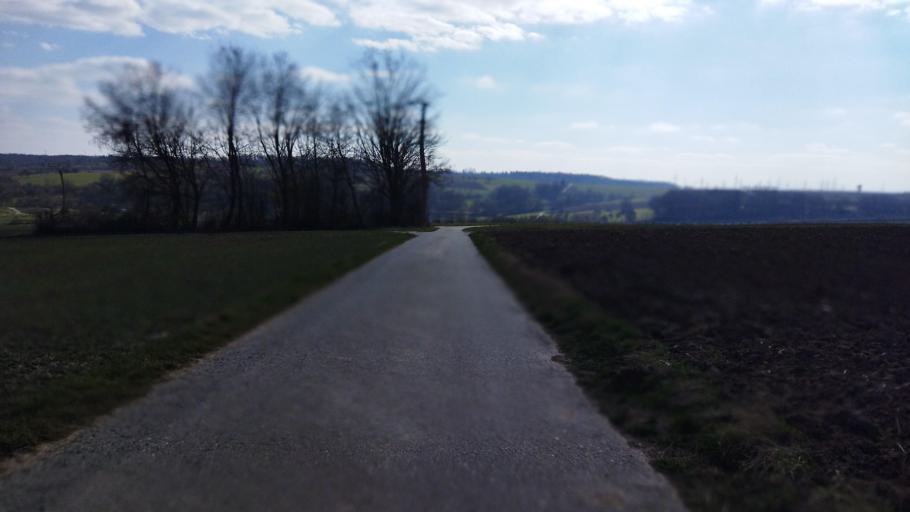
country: DE
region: Baden-Wuerttemberg
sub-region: Regierungsbezirk Stuttgart
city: Ilsfeld
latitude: 49.0592
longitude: 9.2250
